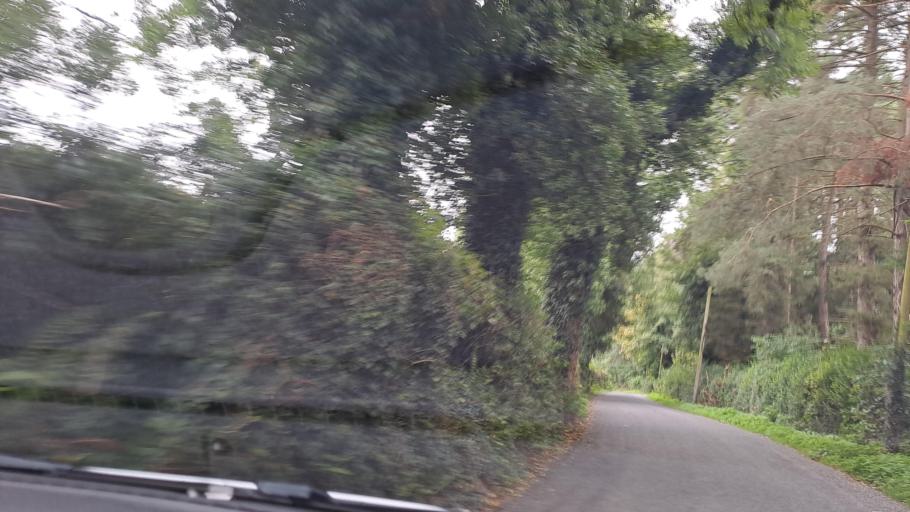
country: IE
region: Ulster
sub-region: County Monaghan
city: Carrickmacross
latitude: 54.0271
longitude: -6.7440
